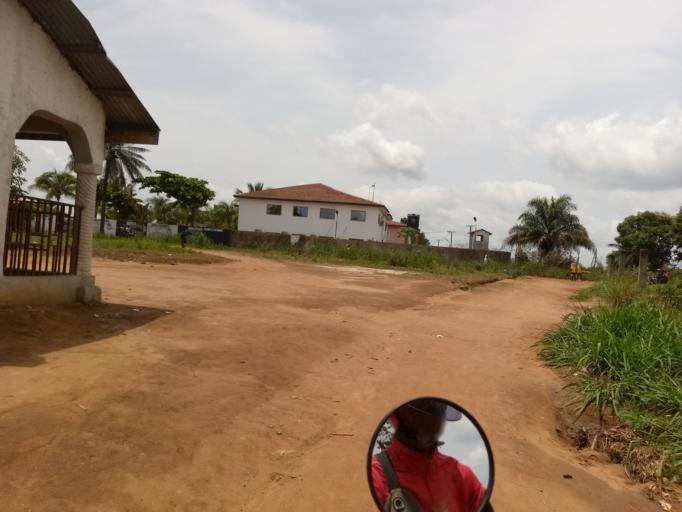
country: SL
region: Western Area
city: Waterloo
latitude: 8.3284
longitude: -13.0400
